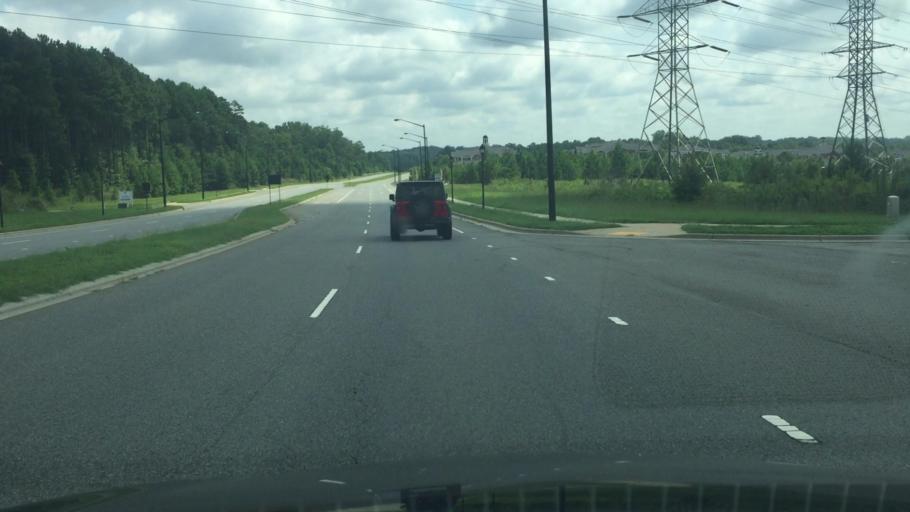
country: US
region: North Carolina
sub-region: Cabarrus County
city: Kannapolis
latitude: 35.4699
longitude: -80.6687
